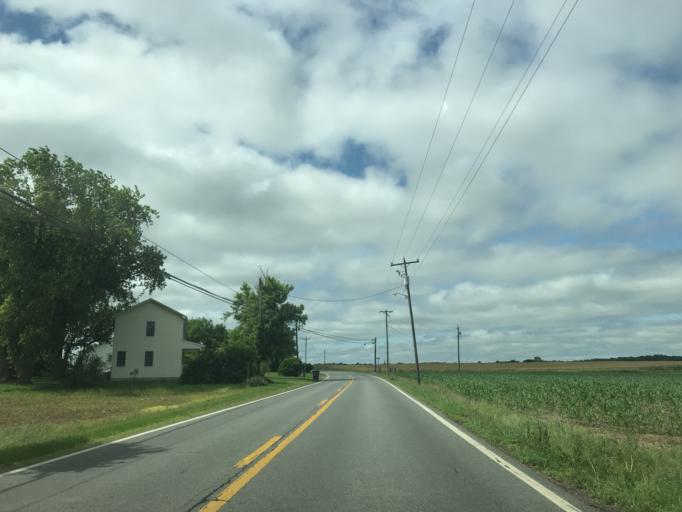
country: US
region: Maryland
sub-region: Caroline County
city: Ridgely
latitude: 38.9078
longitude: -75.9579
